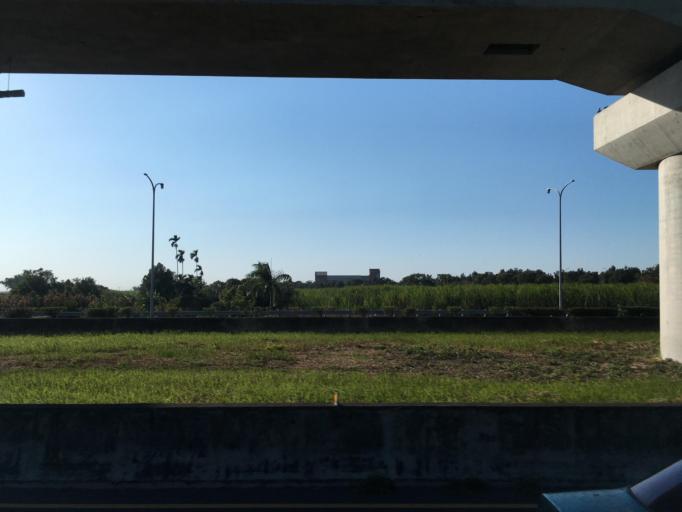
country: TW
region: Taiwan
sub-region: Chiayi
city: Taibao
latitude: 23.4505
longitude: 120.3236
